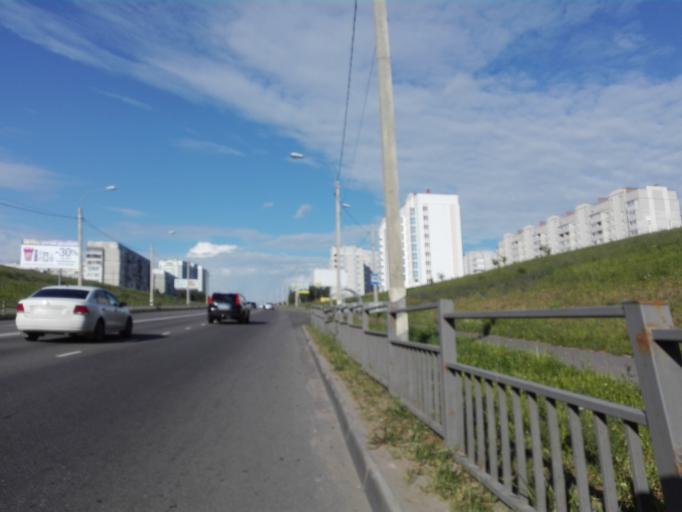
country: RU
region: Orjol
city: Orel
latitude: 53.0015
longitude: 36.1064
